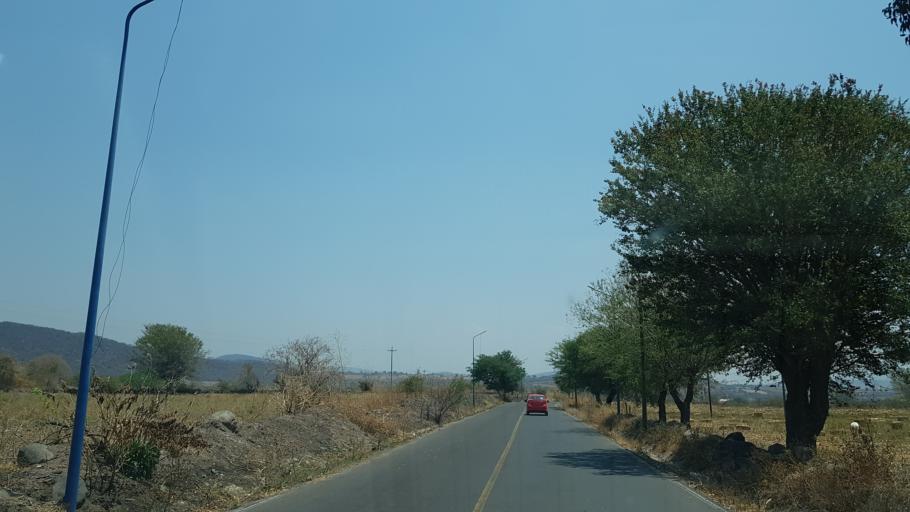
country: MX
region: Puebla
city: Huaquechula
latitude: 18.7669
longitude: -98.5345
